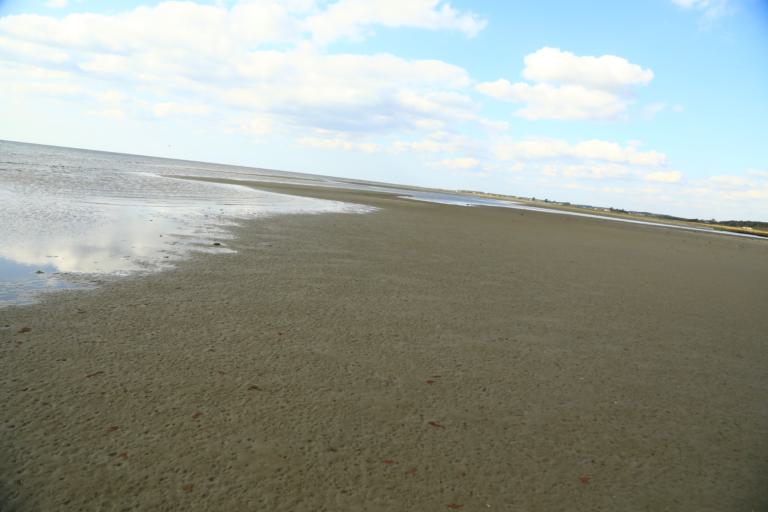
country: SE
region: Halland
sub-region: Varbergs Kommun
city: Tvaaker
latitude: 57.0091
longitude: 12.3441
